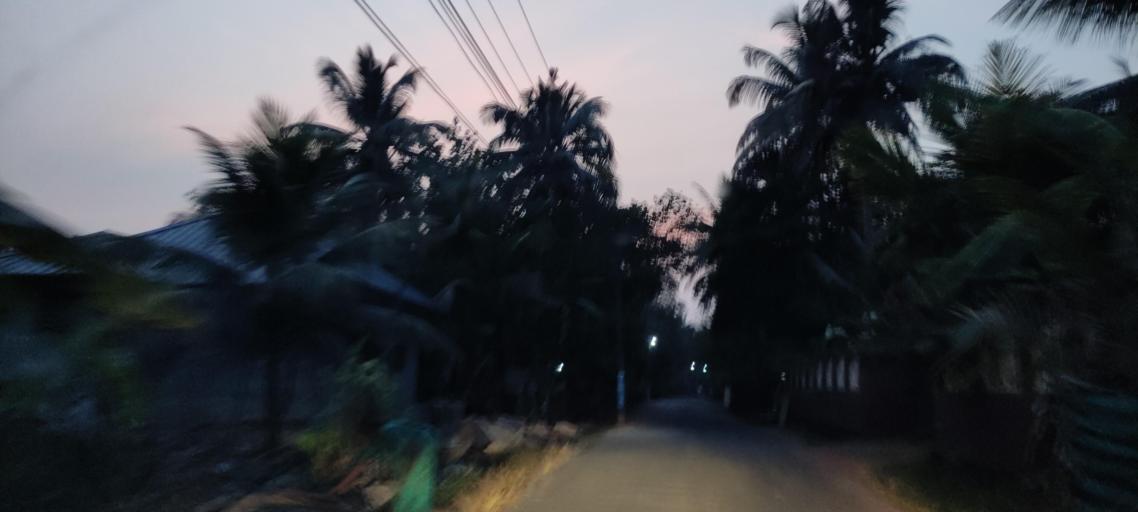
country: IN
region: Kerala
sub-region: Alappuzha
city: Mavelikara
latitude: 9.3211
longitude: 76.4530
